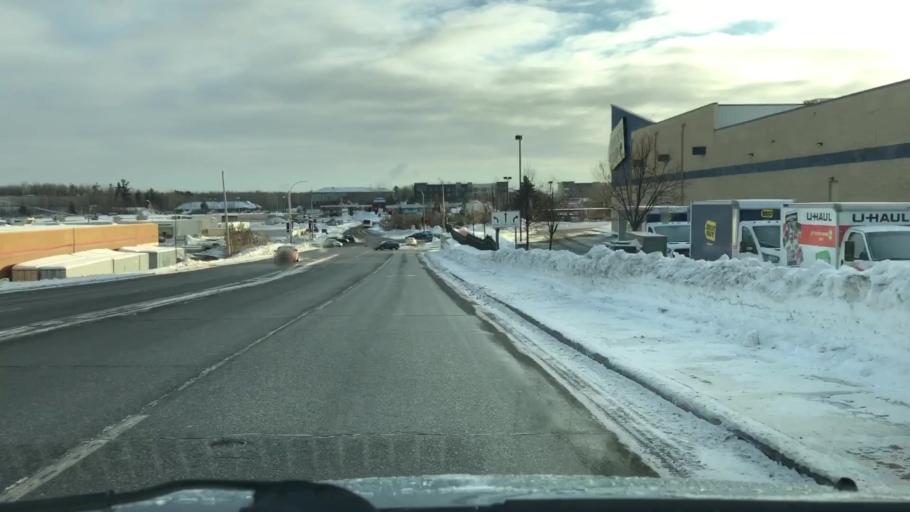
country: US
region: Minnesota
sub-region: Saint Louis County
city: Duluth
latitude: 46.8092
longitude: -92.1694
